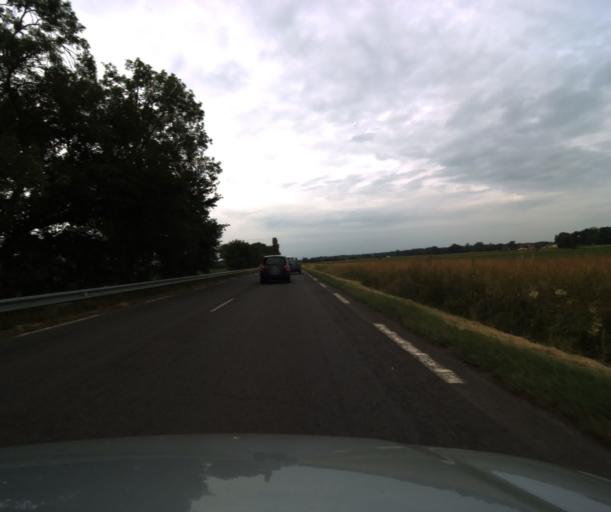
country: FR
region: Midi-Pyrenees
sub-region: Departement des Hautes-Pyrenees
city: Rabastens-de-Bigorre
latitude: 43.3520
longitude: 0.1373
